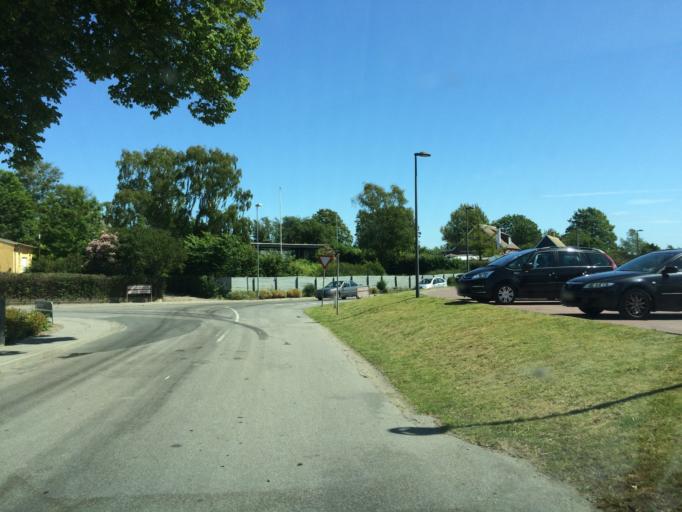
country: DK
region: Central Jutland
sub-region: Samso Kommune
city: Tranebjerg
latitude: 55.8285
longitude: 10.5946
